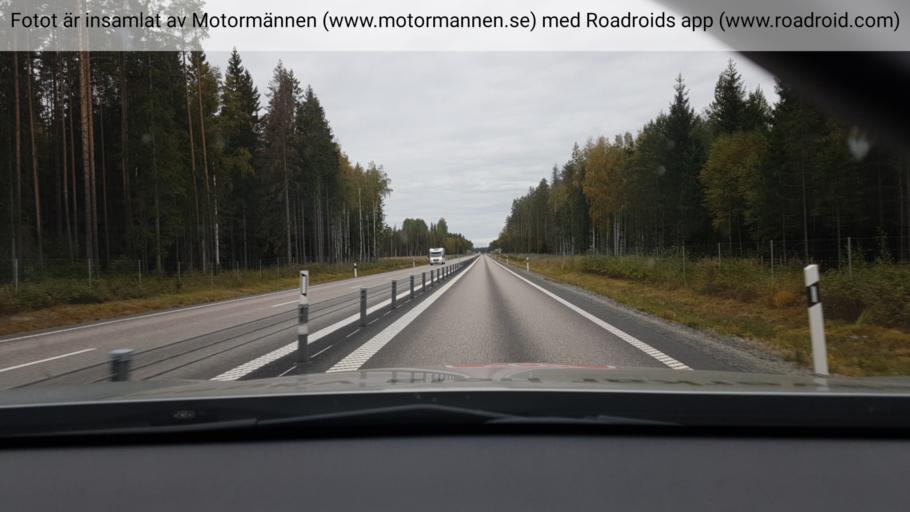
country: SE
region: Uppsala
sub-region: Heby Kommun
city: Tarnsjo
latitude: 60.0570
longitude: 16.8950
